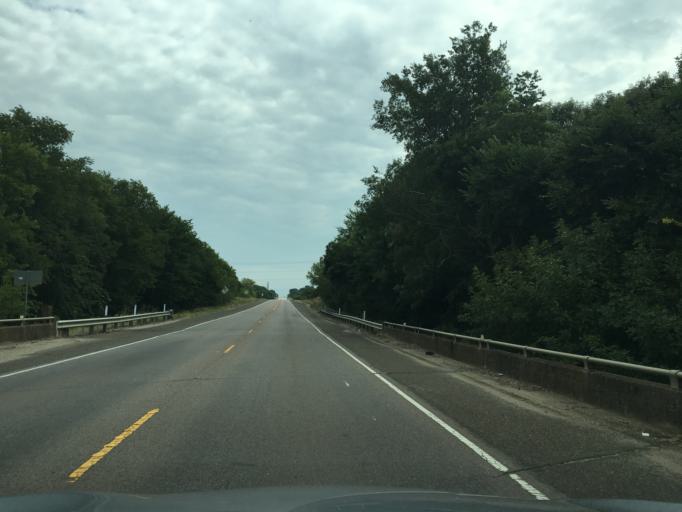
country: US
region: Texas
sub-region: Collin County
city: Anna
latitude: 33.3176
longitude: -96.5046
